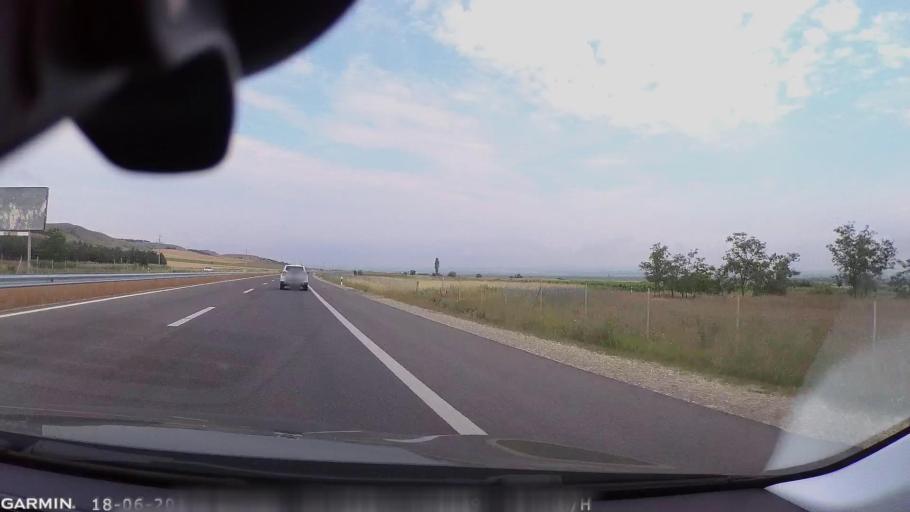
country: MK
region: Stip
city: Shtip
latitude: 41.7978
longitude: 22.0845
